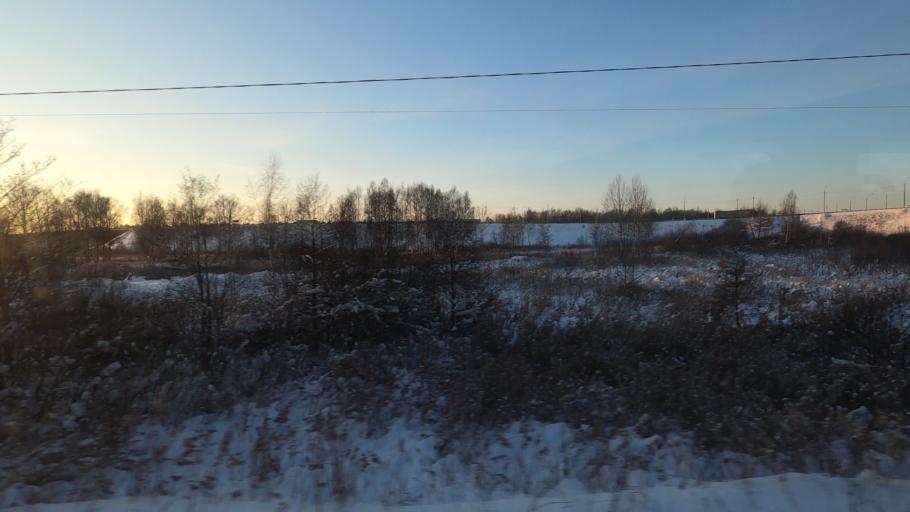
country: RU
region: Moskovskaya
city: Orud'yevo
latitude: 56.4074
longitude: 37.4953
